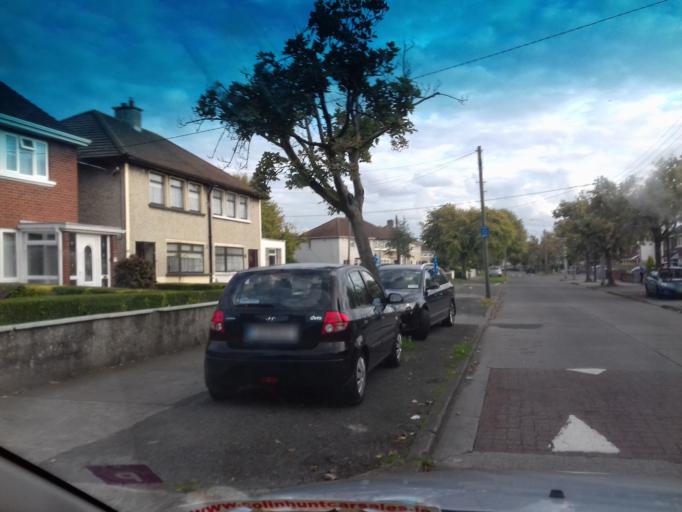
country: IE
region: Leinster
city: Beaumont
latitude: 53.3904
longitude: -6.2354
